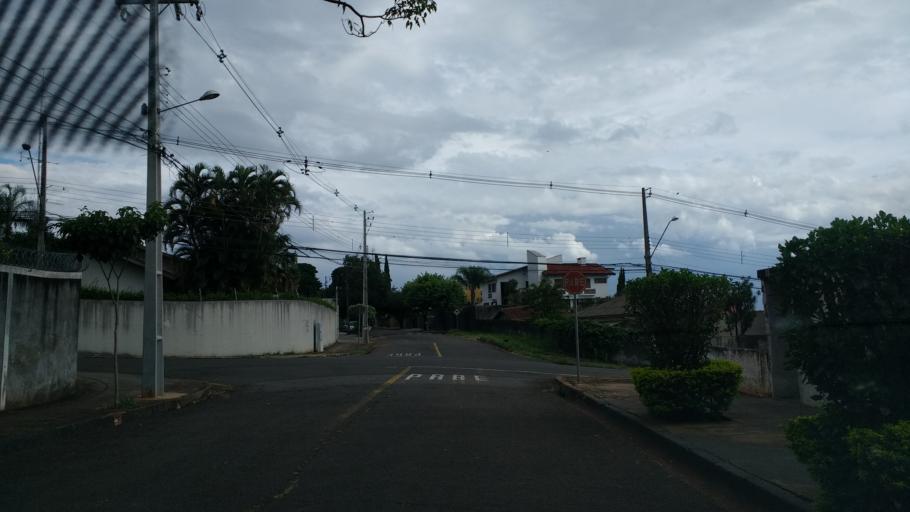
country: BR
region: Parana
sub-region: Londrina
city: Londrina
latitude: -23.3116
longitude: -51.1807
